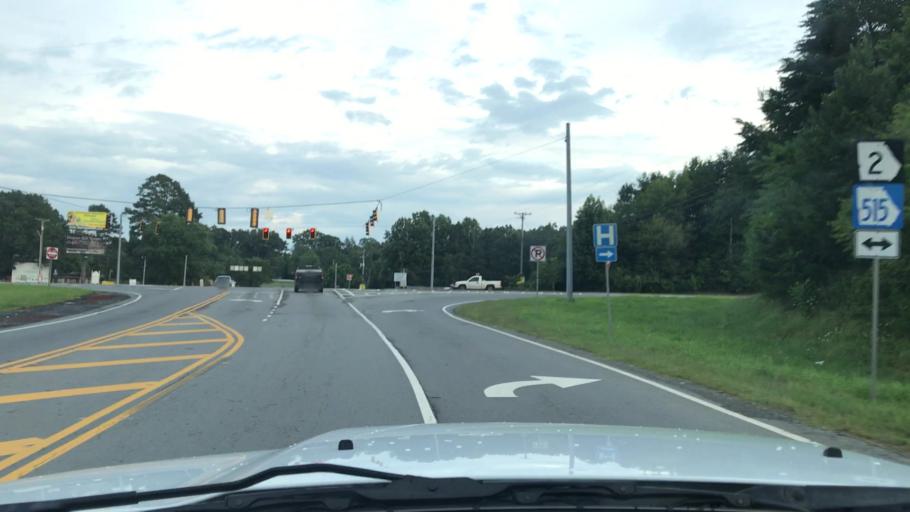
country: US
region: Georgia
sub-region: Fannin County
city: Blue Ridge
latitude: 34.8938
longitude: -84.2622
